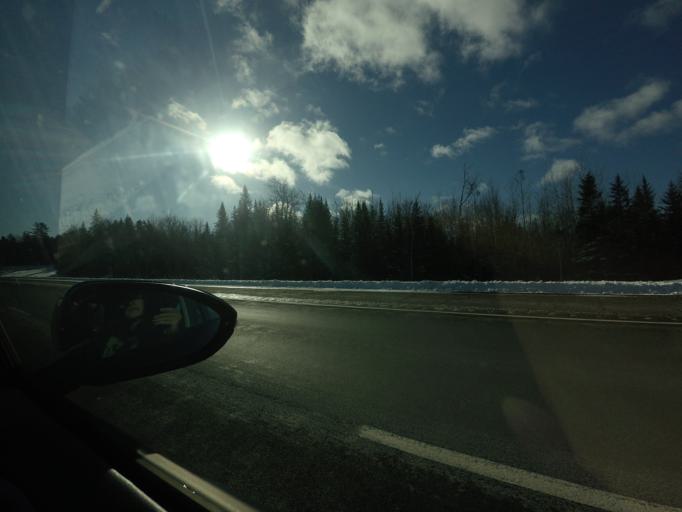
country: CA
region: New Brunswick
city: Fredericton
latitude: 45.8768
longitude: -66.6318
